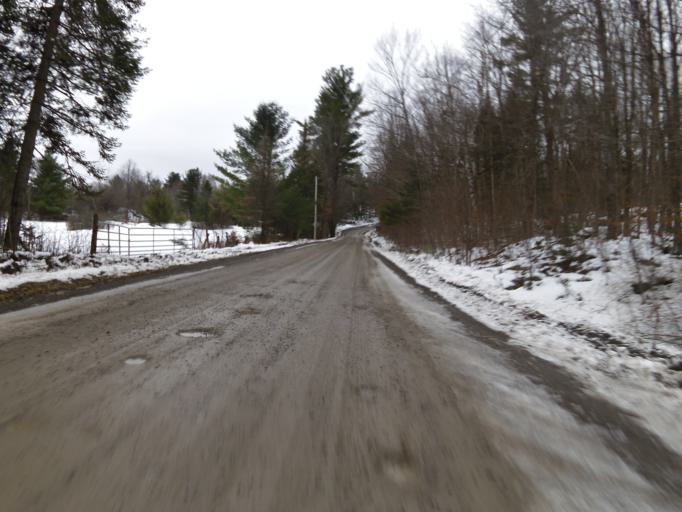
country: CA
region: Ontario
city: Carleton Place
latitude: 45.1853
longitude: -76.2234
